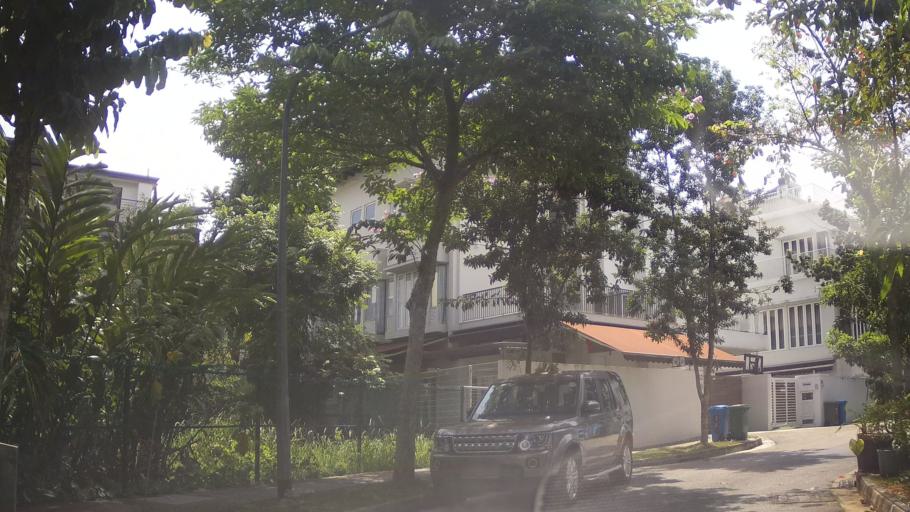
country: MY
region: Johor
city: Johor Bahru
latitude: 1.3679
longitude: 103.7710
